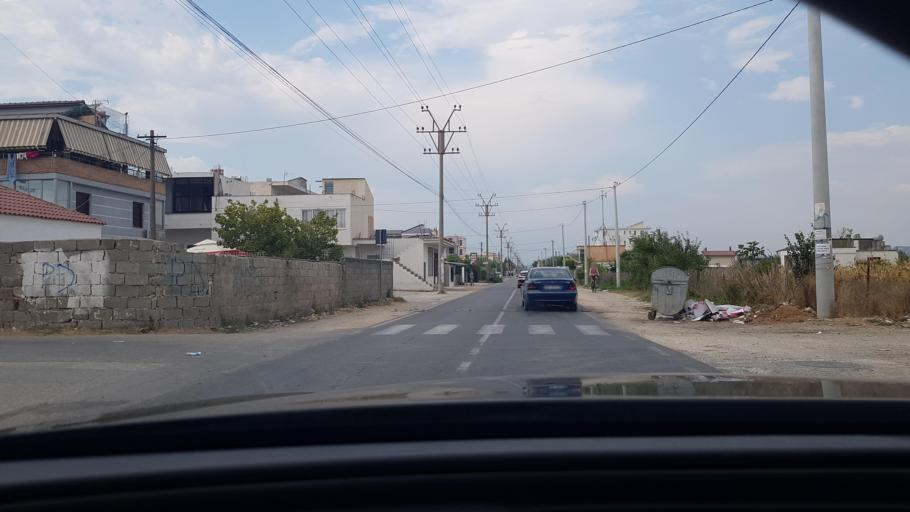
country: AL
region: Durres
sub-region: Rrethi i Durresit
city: Sukth
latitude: 41.3964
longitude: 19.5466
